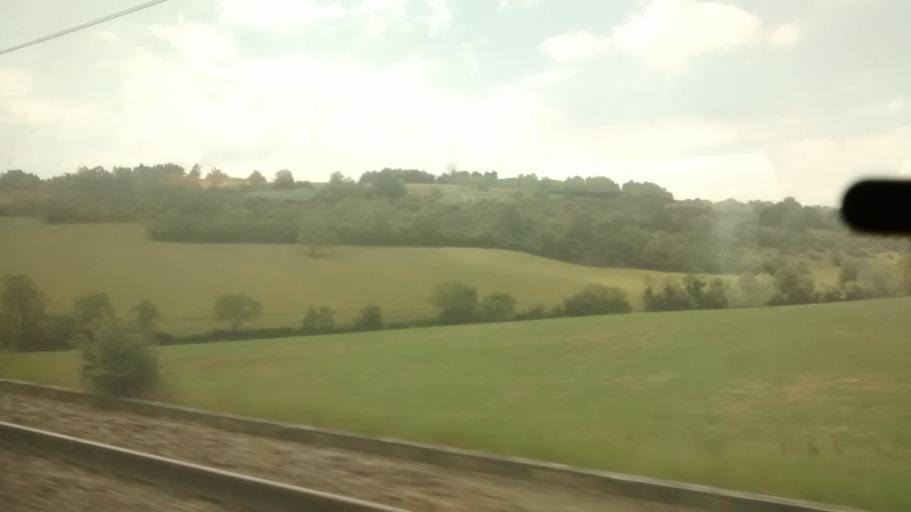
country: FR
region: Bourgogne
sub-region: Departement de Saone-et-Loire
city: Saint-Gengoux-le-National
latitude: 46.5750
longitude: 4.6181
